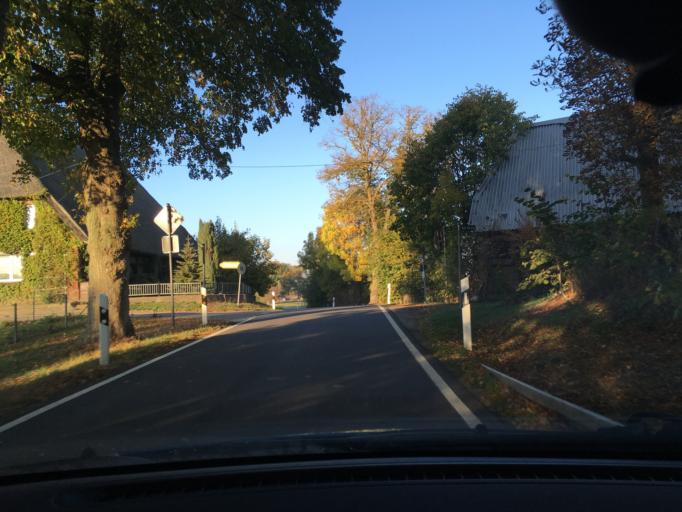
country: DE
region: Lower Saxony
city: Bleckede
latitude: 53.3169
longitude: 10.7926
